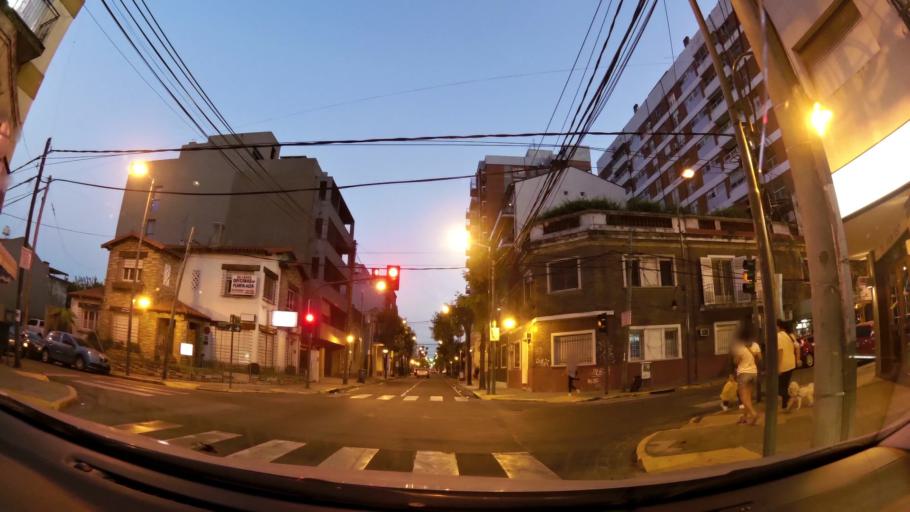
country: AR
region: Buenos Aires
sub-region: Partido de Tigre
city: Tigre
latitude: -34.4405
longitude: -58.5559
